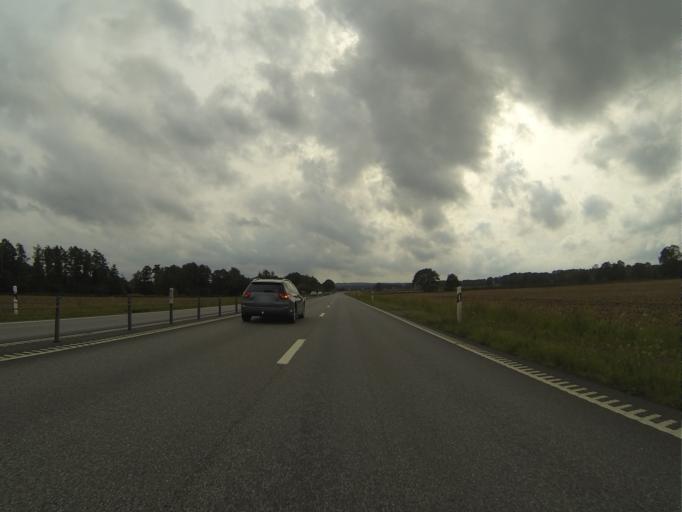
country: SE
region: Skane
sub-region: Kristianstads Kommun
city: Degeberga
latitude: 55.9393
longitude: 14.0432
